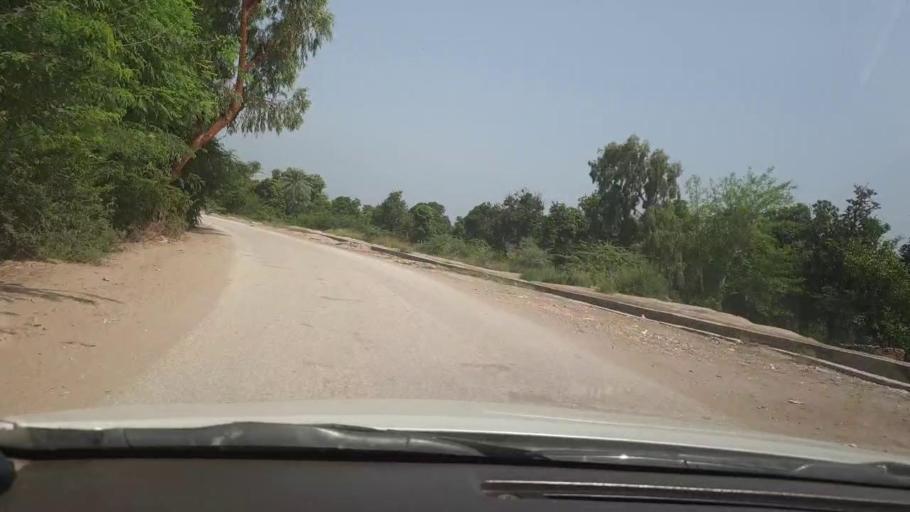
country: PK
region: Sindh
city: Shikarpur
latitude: 27.9410
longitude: 68.6402
